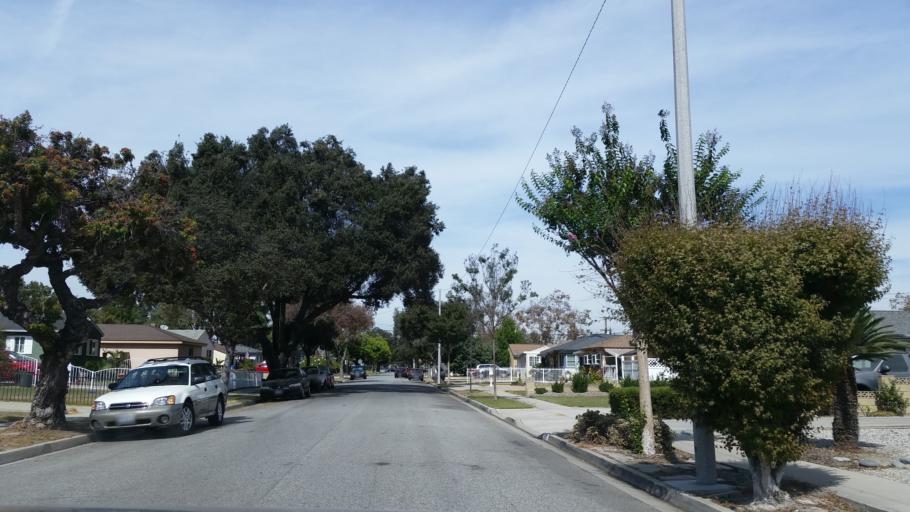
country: US
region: California
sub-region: Los Angeles County
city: Lakewood
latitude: 33.8630
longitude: -118.1318
